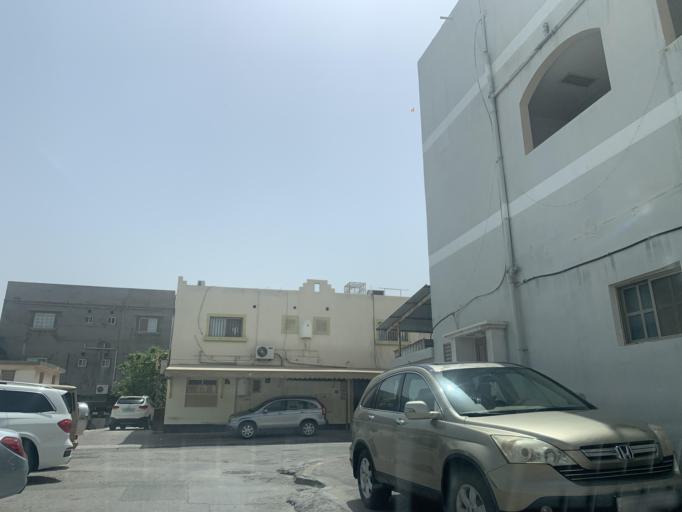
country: BH
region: Northern
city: Madinat `Isa
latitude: 26.1510
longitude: 50.5253
